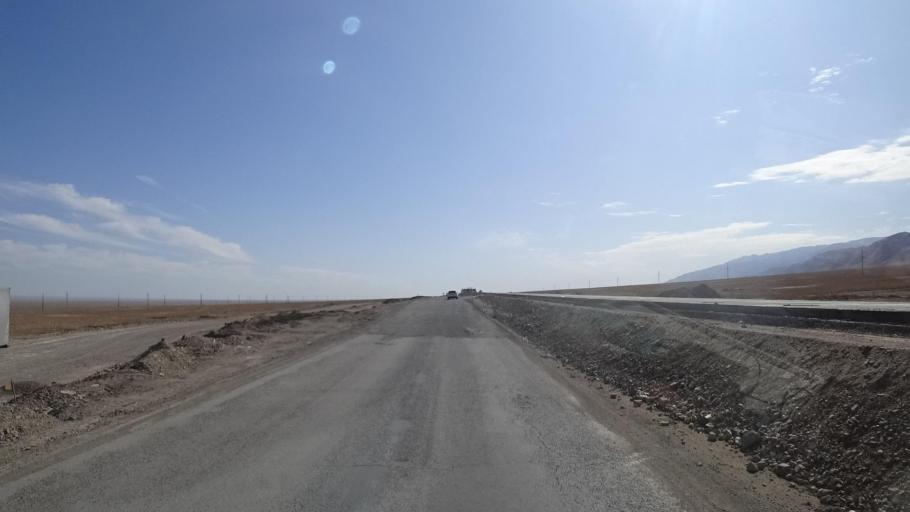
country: KG
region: Chuy
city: Ivanovka
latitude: 43.3849
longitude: 75.1696
